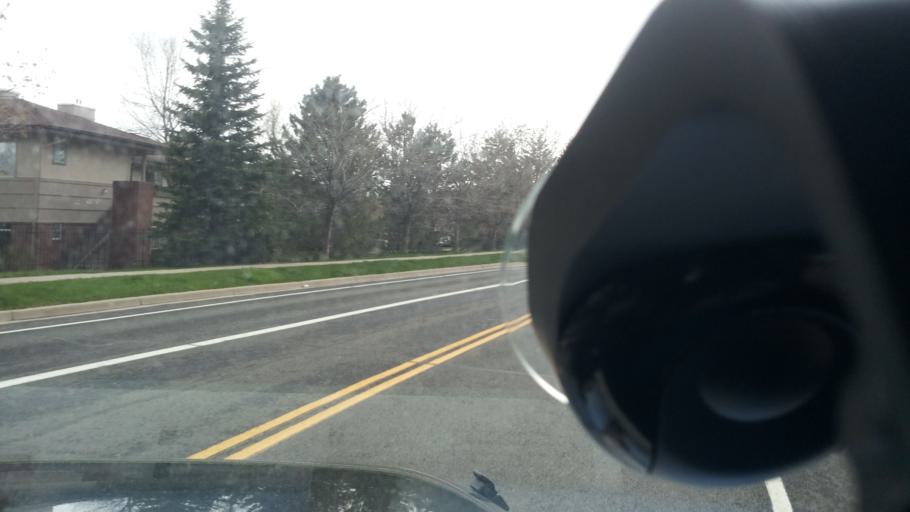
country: US
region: Colorado
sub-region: Boulder County
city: Superior
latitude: 39.9607
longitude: -105.1593
